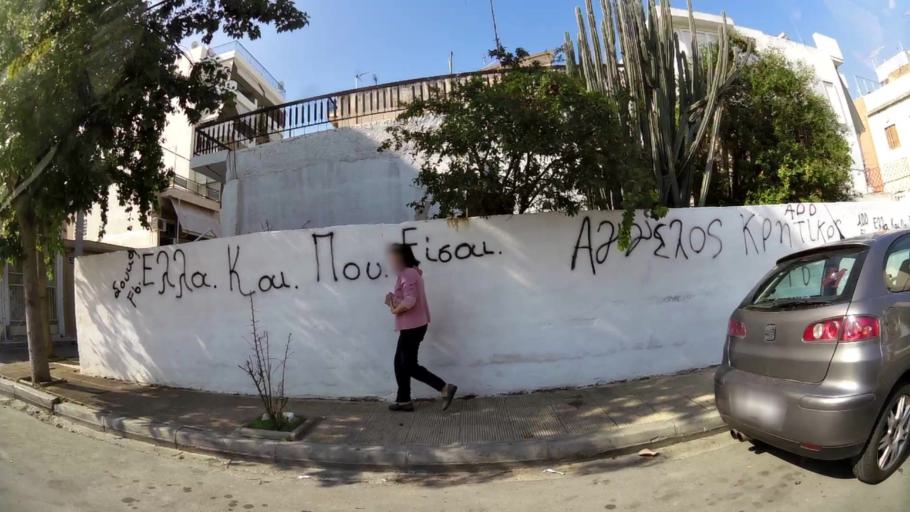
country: GR
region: Attica
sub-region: Nomos Piraios
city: Drapetsona
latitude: 37.9509
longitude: 23.6300
